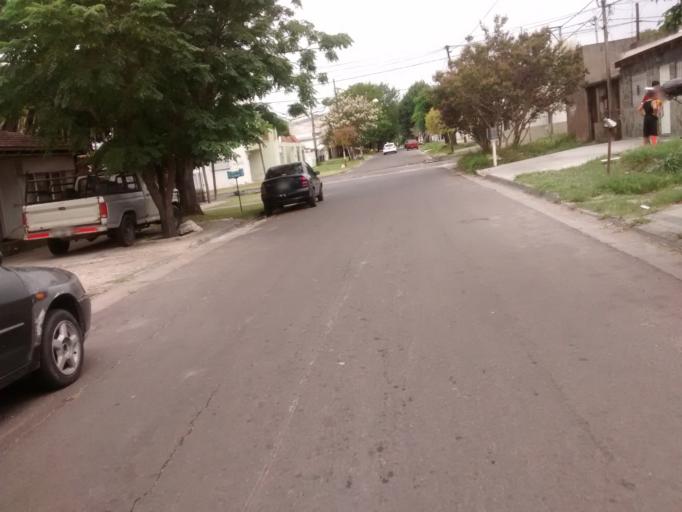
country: AR
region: Buenos Aires
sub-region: Partido de La Plata
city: La Plata
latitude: -34.9339
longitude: -57.9194
